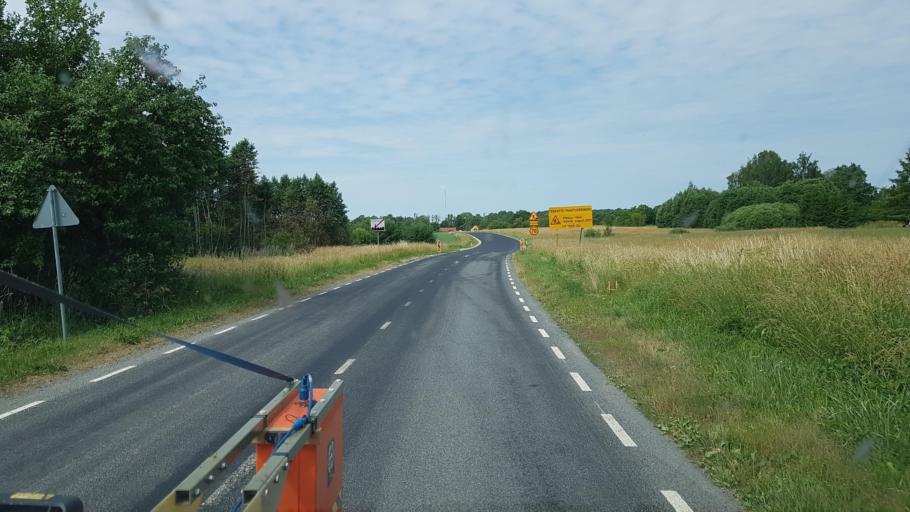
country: EE
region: Paernumaa
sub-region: Halinga vald
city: Parnu-Jaagupi
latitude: 58.6217
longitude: 24.3888
